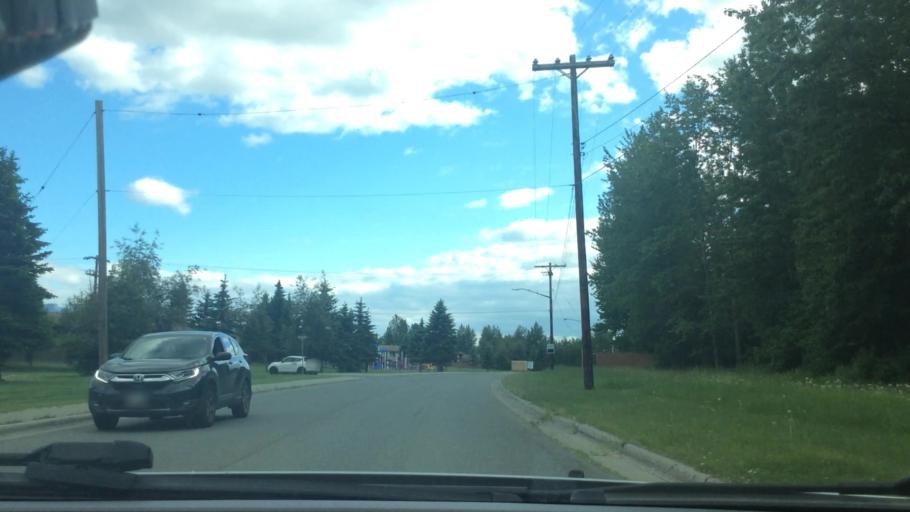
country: US
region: Alaska
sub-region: Anchorage Municipality
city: Elmendorf Air Force Base
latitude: 61.2305
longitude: -149.7556
